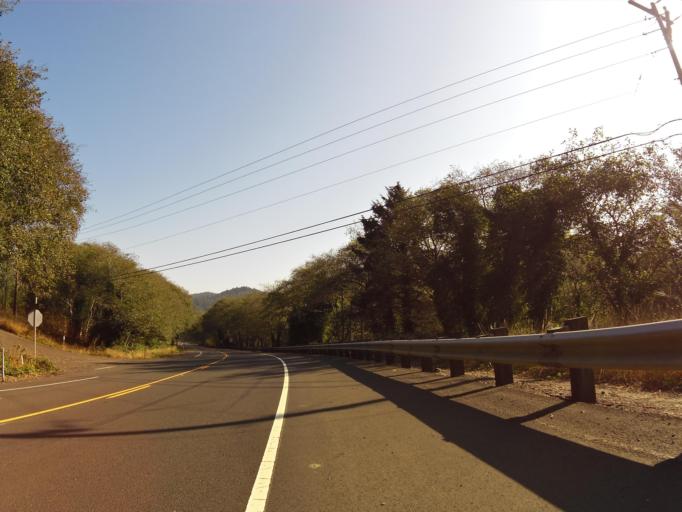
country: US
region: Oregon
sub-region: Tillamook County
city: Pacific City
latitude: 45.1008
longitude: -123.9819
